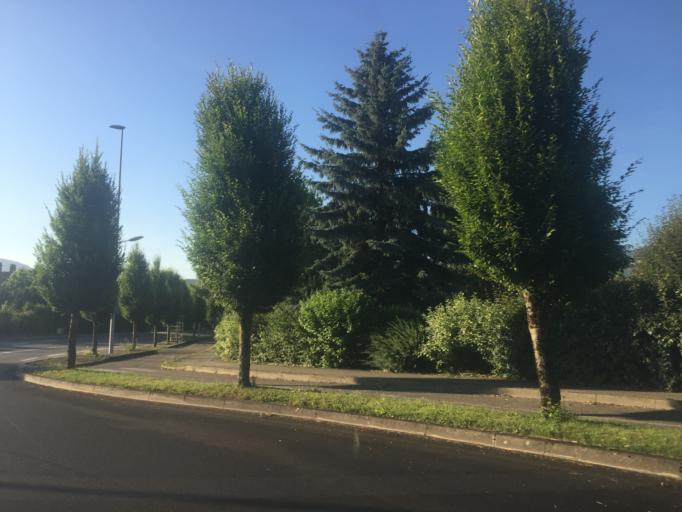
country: FR
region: Rhone-Alpes
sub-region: Departement de la Savoie
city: Cognin
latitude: 45.5720
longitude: 5.8902
